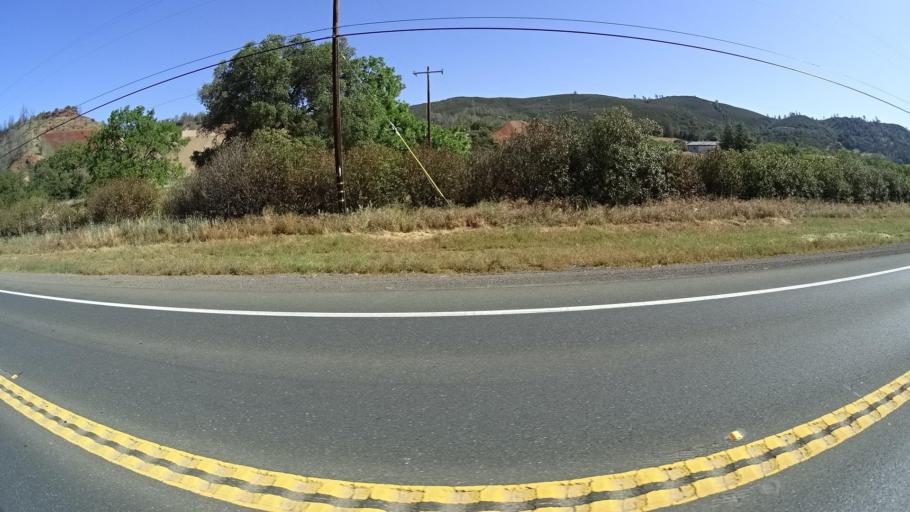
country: US
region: California
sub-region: Lake County
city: Clearlake Oaks
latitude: 39.0129
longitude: -122.6318
